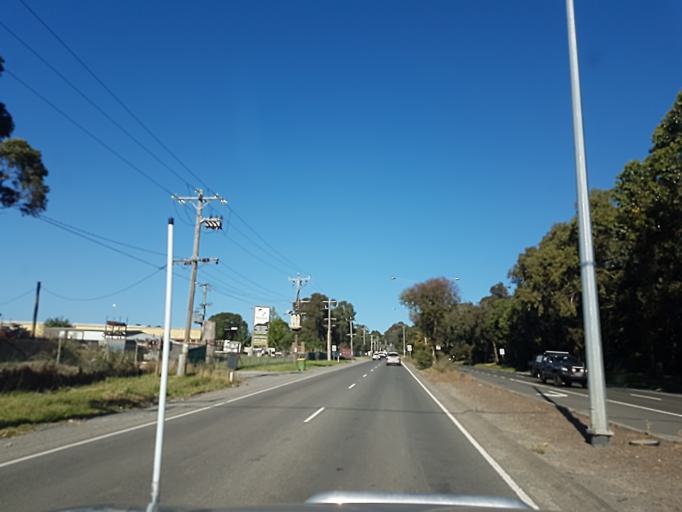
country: AU
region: Victoria
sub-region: Maroondah
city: Kilsyth South
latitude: -37.8162
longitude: 145.3236
